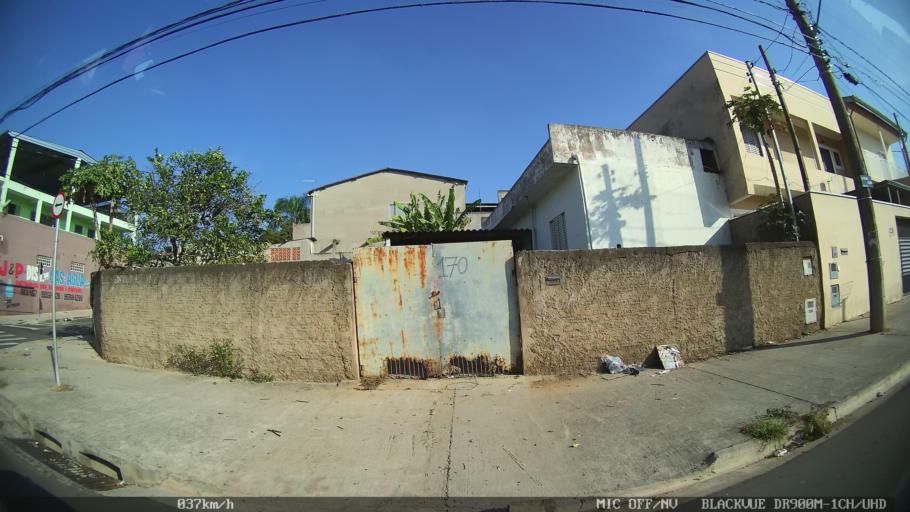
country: BR
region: Sao Paulo
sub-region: Campinas
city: Campinas
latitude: -22.9855
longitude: -47.1319
